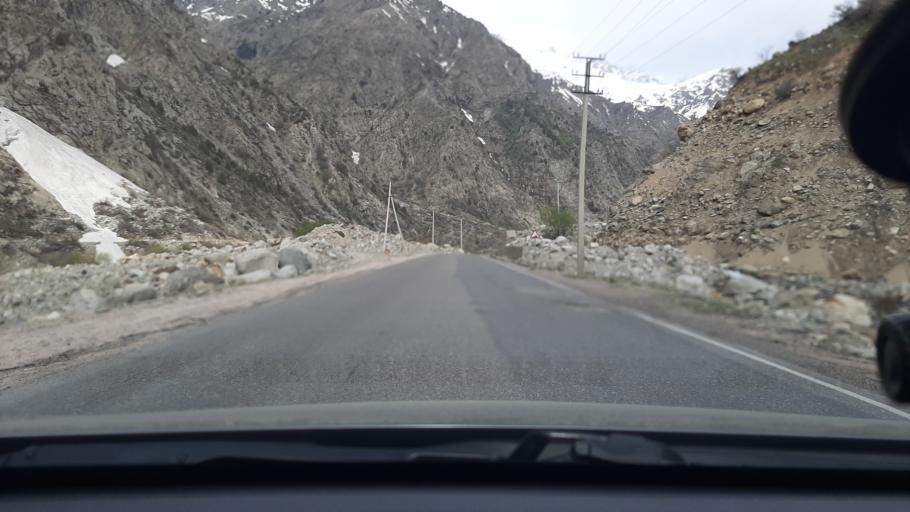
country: TJ
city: Tagob
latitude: 38.9146
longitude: 68.8187
